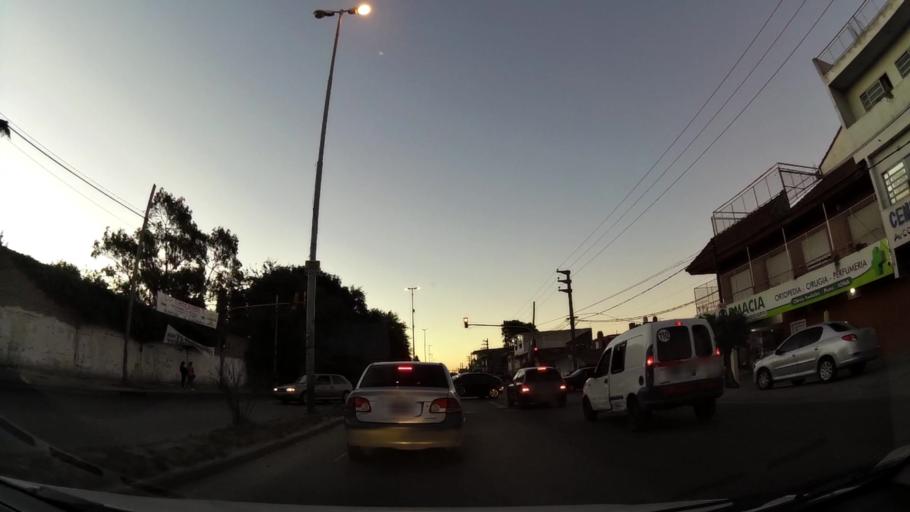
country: AR
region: Buenos Aires
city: San Justo
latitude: -34.7171
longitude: -58.6000
